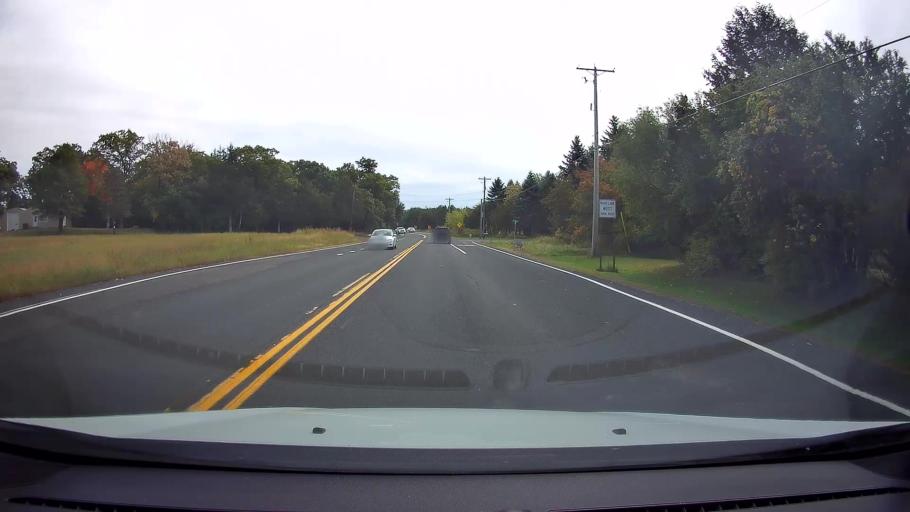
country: US
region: Minnesota
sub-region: Washington County
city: Grant
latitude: 45.0856
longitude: -92.9305
